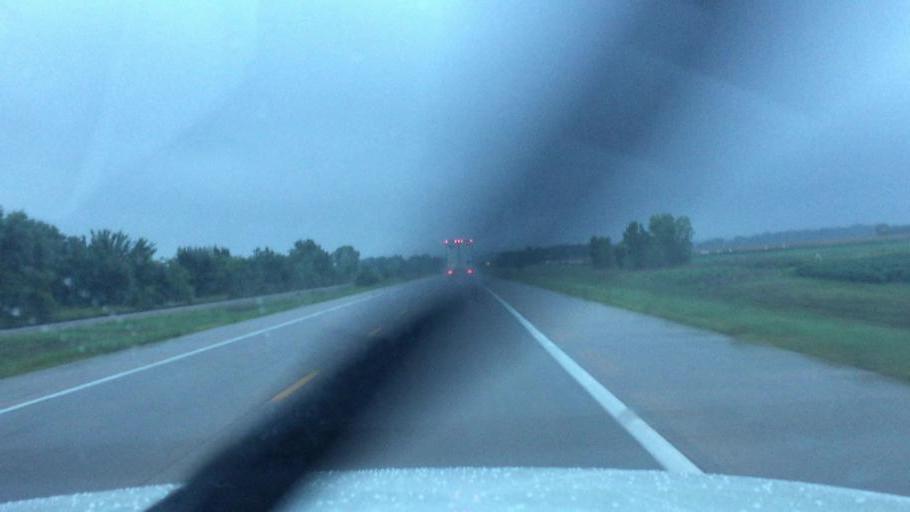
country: US
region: Kansas
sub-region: Neosho County
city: Chanute
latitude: 37.5664
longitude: -95.4712
